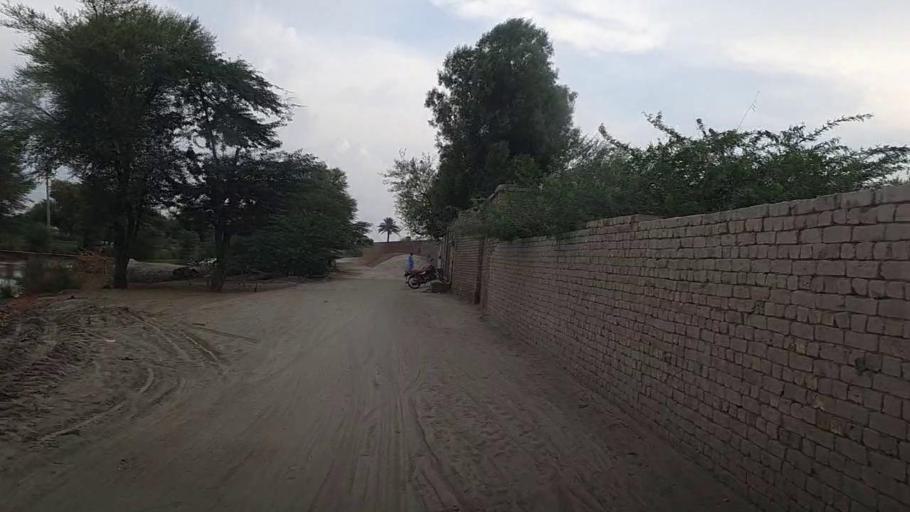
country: PK
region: Sindh
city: Khanpur
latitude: 27.8429
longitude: 69.4161
